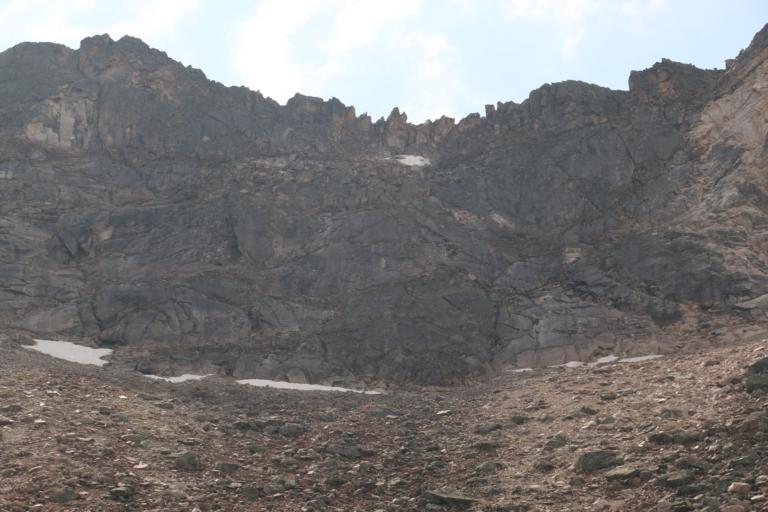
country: RU
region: Respublika Buryatiya
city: Novyy Uoyan
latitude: 56.3152
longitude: 111.2662
